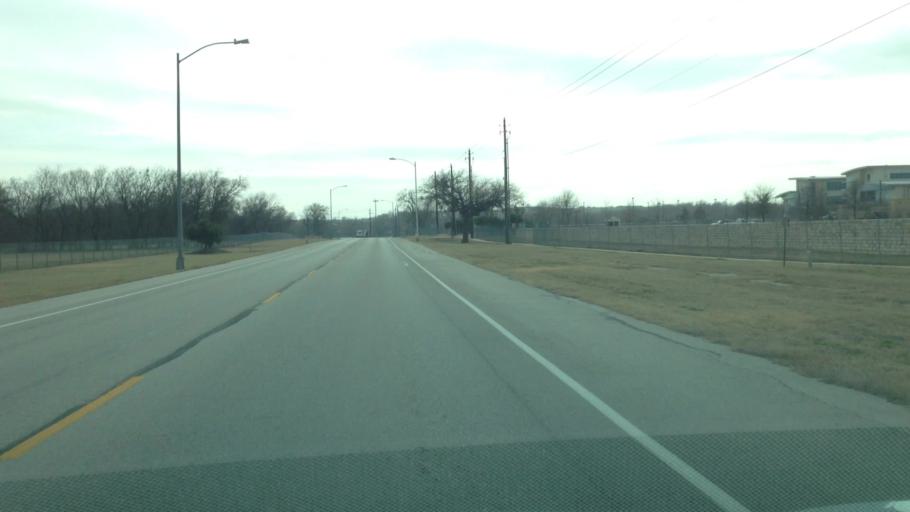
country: US
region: Texas
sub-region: Travis County
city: Hornsby Bend
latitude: 30.1767
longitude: -97.6686
